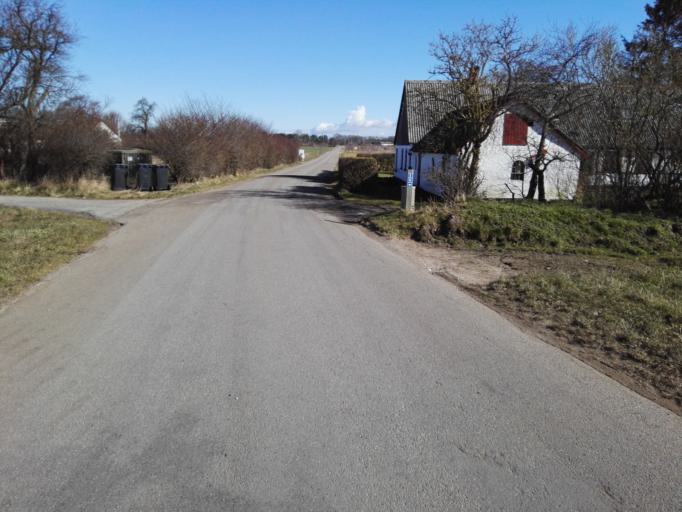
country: DK
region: Zealand
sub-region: Lejre Kommune
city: Ejby
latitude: 55.7748
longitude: 11.8209
